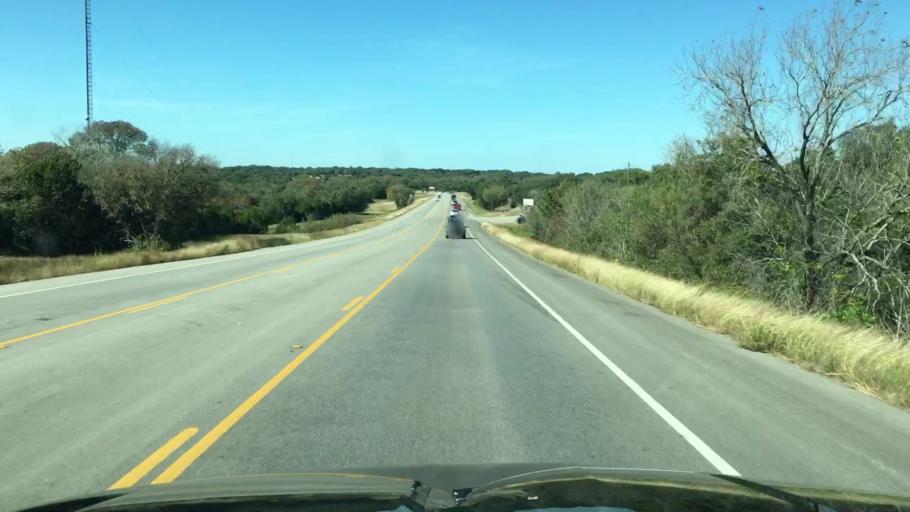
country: US
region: Texas
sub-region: Hays County
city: Dripping Springs
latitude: 30.2003
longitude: -98.1888
